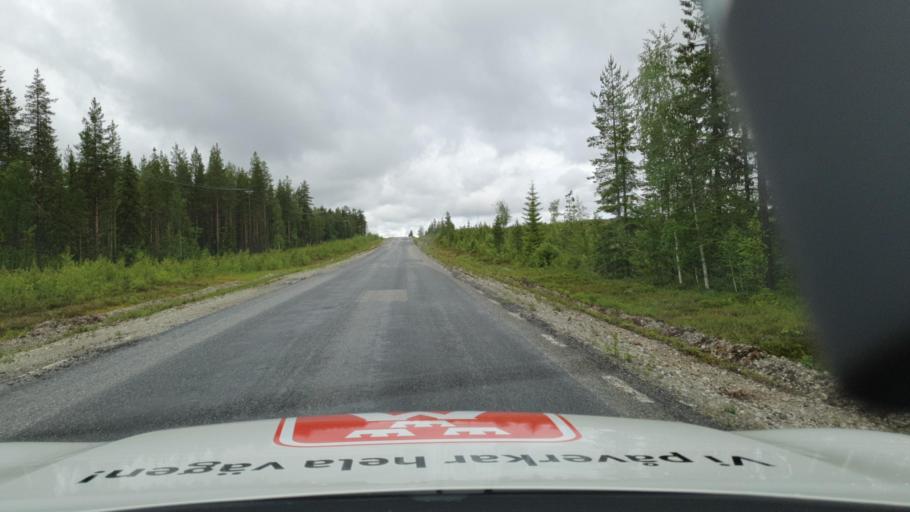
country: SE
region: Vaesterbotten
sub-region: Dorotea Kommun
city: Dorotea
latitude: 64.1611
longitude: 16.6499
